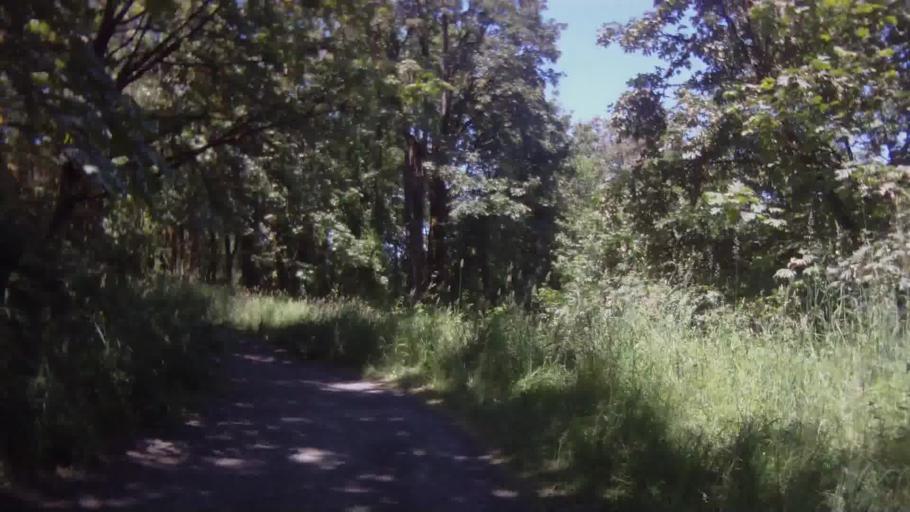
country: US
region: Oregon
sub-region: Washington County
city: West Haven
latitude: 45.5577
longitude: -122.7457
